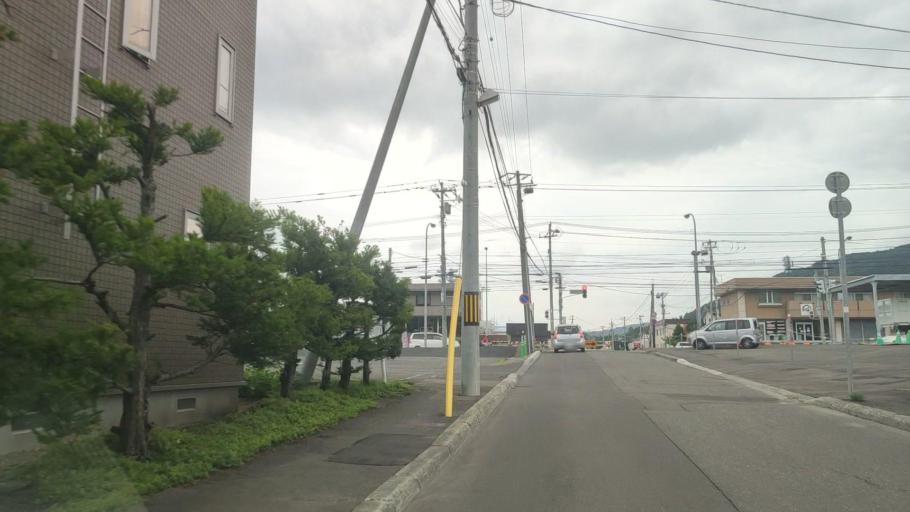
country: JP
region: Hokkaido
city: Sapporo
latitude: 42.9623
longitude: 141.3187
